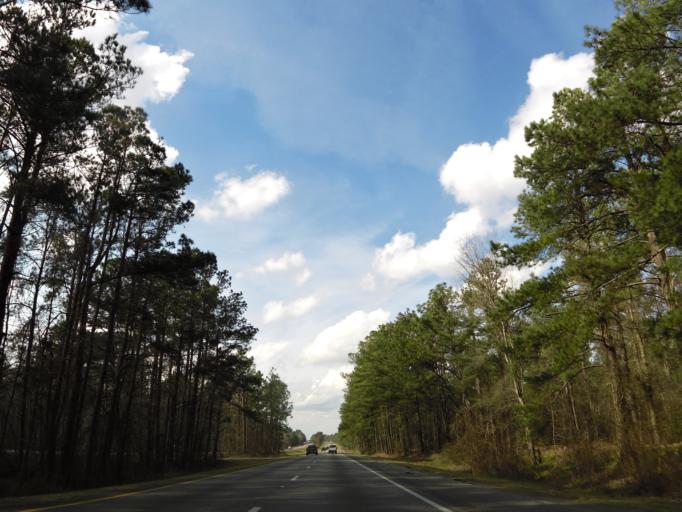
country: US
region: South Carolina
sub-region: Dorchester County
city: Ridgeville
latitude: 33.1635
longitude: -80.3570
